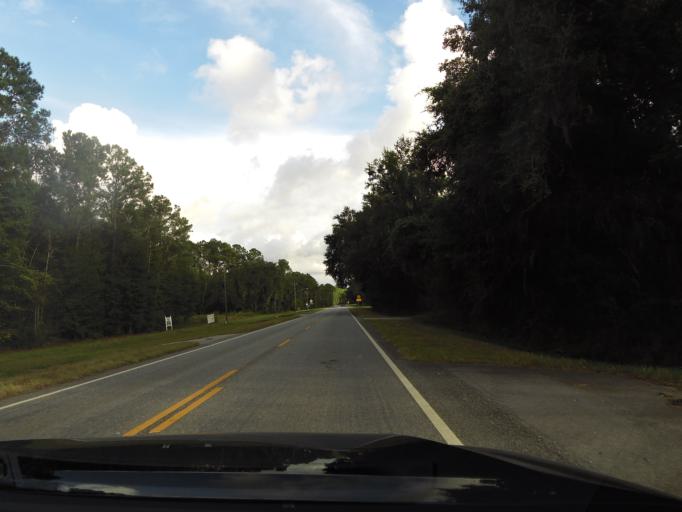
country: US
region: Georgia
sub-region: Liberty County
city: Midway
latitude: 31.7240
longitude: -81.4211
